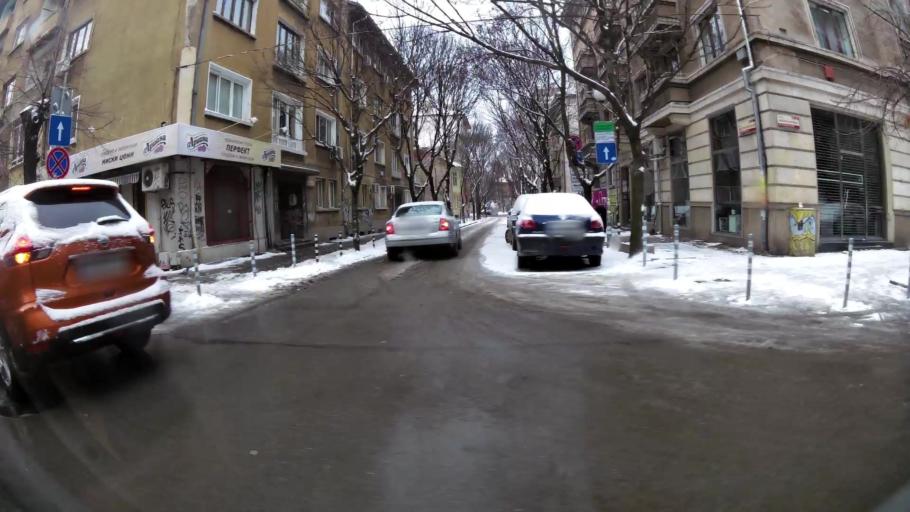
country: BG
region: Sofia-Capital
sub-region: Stolichna Obshtina
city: Sofia
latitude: 42.6869
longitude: 23.3284
